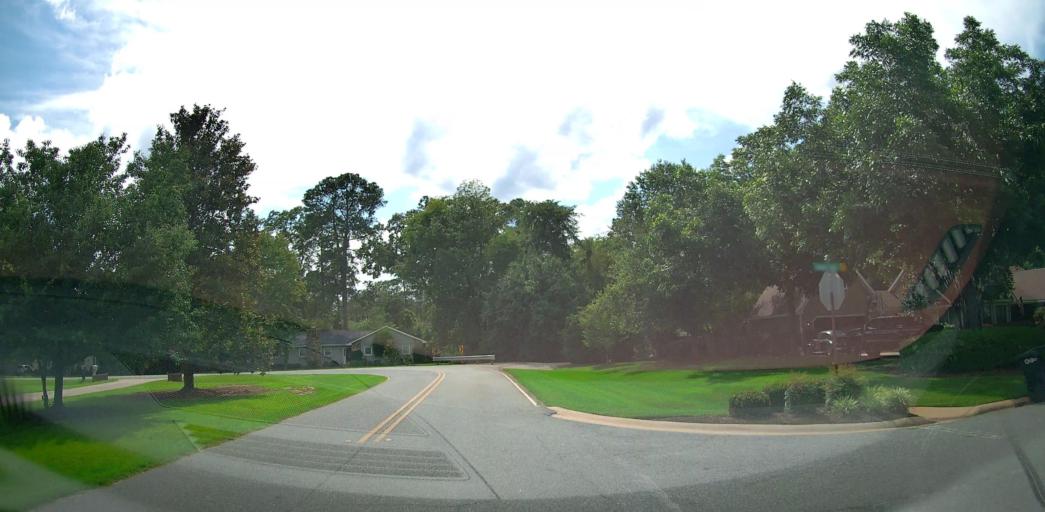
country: US
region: Georgia
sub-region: Houston County
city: Centerville
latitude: 32.5840
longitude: -83.6677
